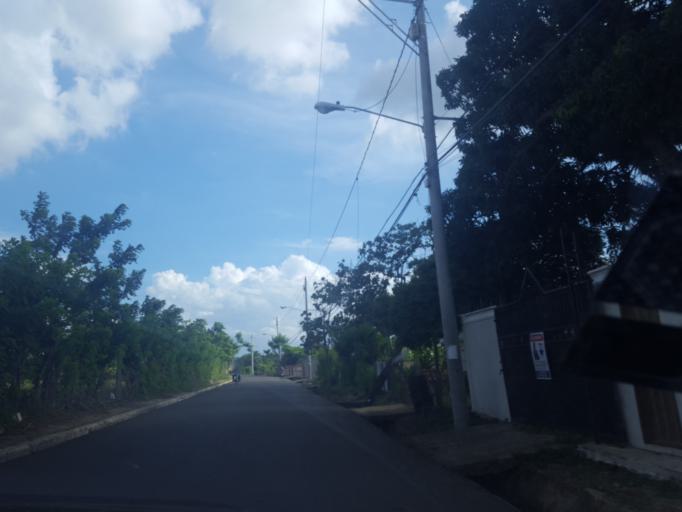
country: DO
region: Santiago
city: Licey al Medio
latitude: 19.3799
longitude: -70.6224
